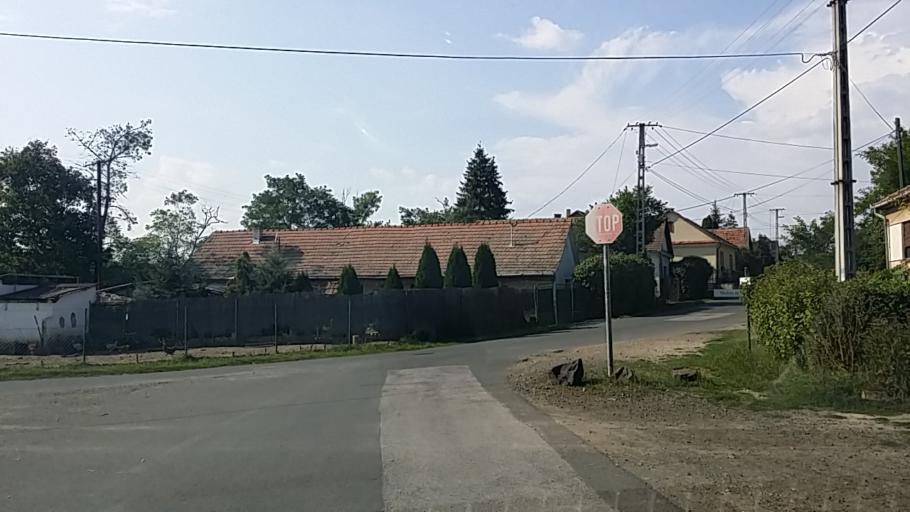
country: HU
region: Nograd
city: Bujak
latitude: 47.8315
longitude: 19.5322
